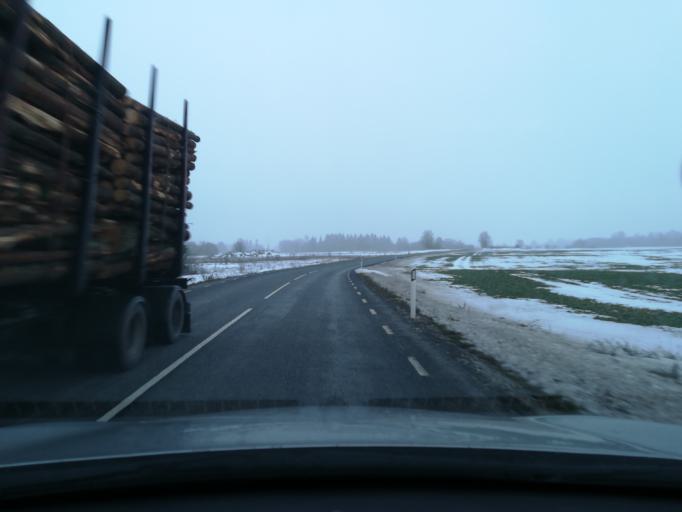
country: EE
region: Harju
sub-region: Raasiku vald
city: Raasiku
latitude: 59.3510
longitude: 25.1315
